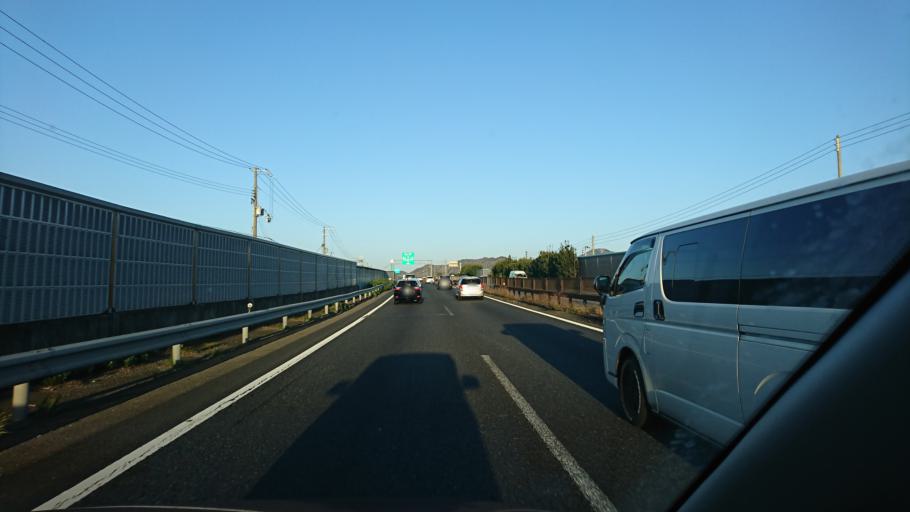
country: JP
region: Hyogo
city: Kakogawacho-honmachi
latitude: 34.7853
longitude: 134.8258
